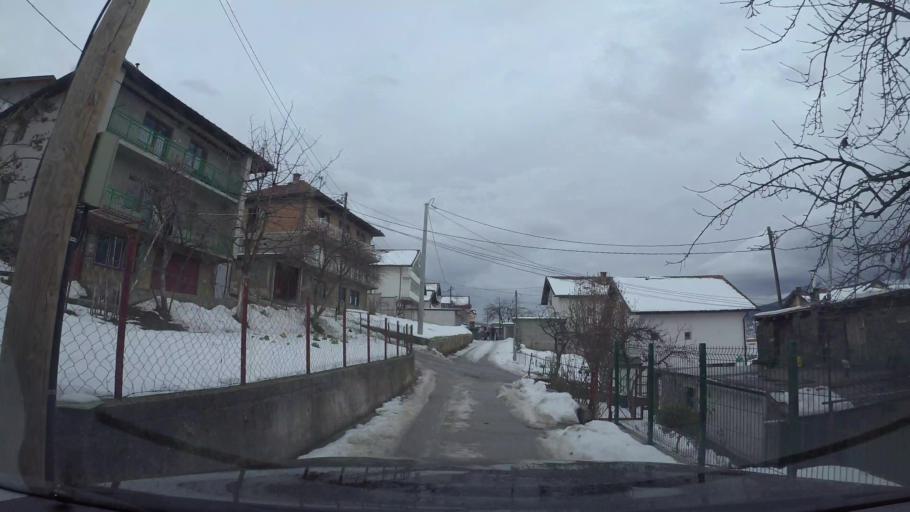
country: BA
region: Federation of Bosnia and Herzegovina
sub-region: Kanton Sarajevo
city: Sarajevo
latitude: 43.8644
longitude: 18.3614
